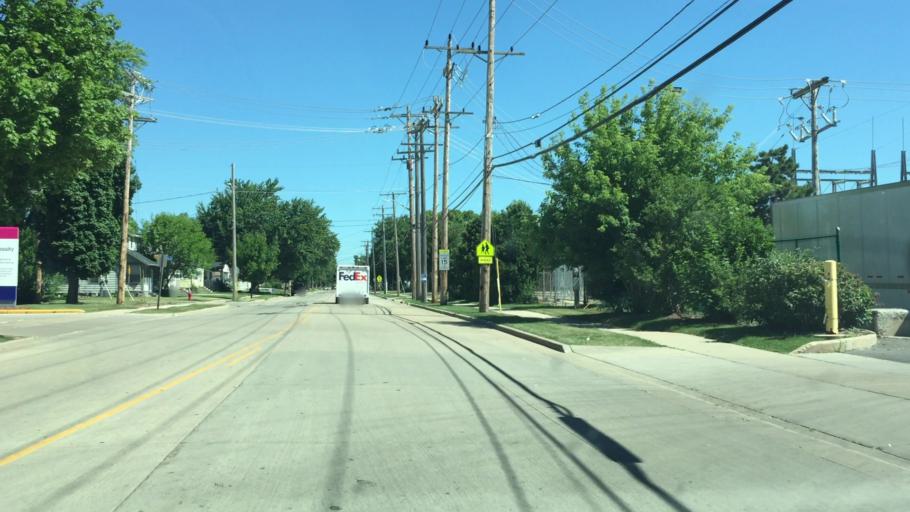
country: US
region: Wisconsin
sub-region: Winnebago County
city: Menasha
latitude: 44.2059
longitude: -88.4531
